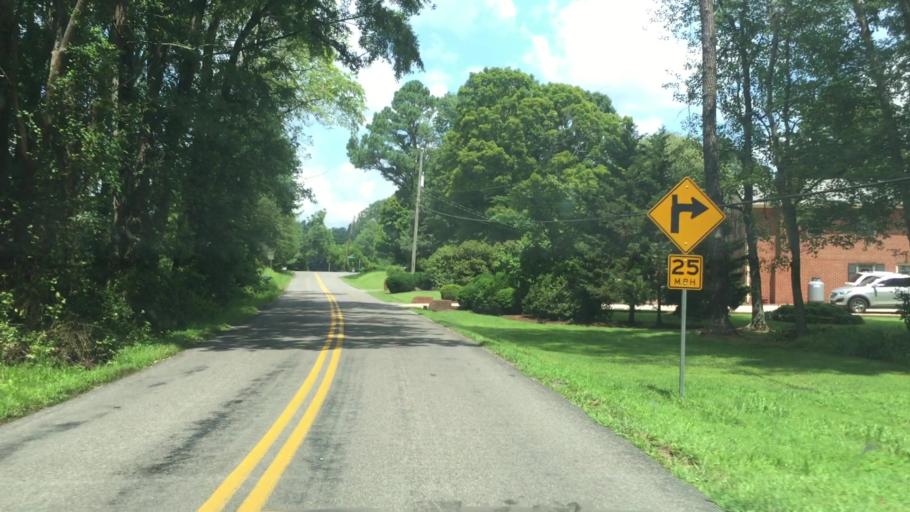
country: US
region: Virginia
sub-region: Hanover County
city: Ashland
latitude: 37.7514
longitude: -77.4980
